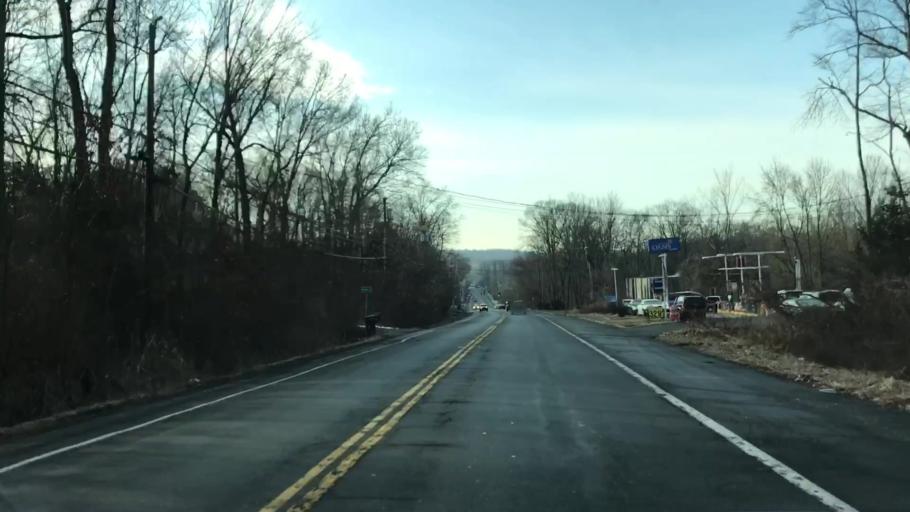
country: US
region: New York
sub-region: Rockland County
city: Congers
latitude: 41.1317
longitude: -73.9397
